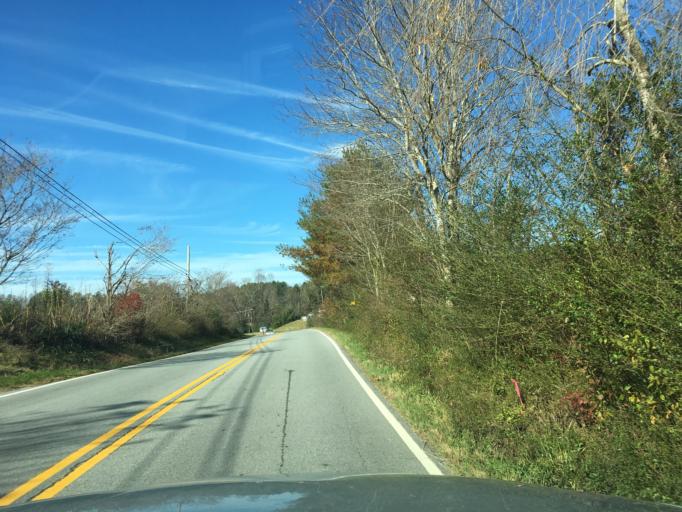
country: US
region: North Carolina
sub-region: Henderson County
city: Etowah
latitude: 35.2398
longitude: -82.6294
